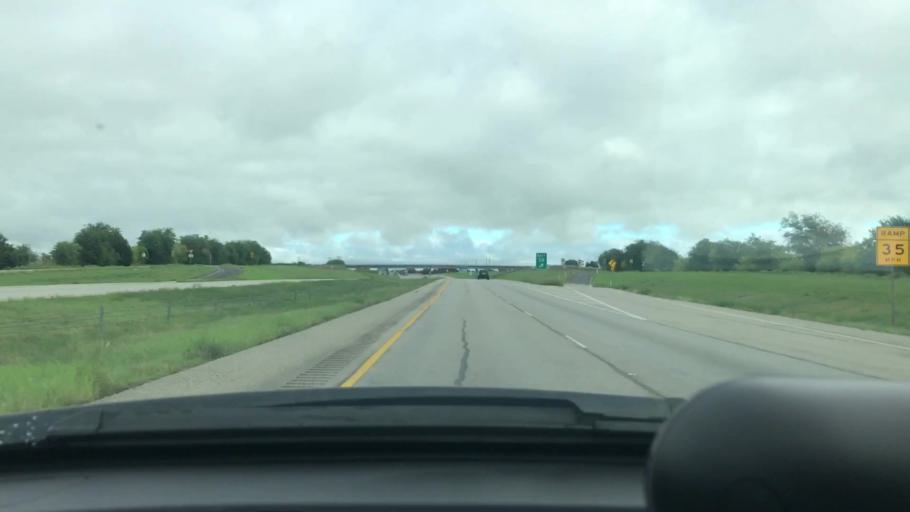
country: US
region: Texas
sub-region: Grayson County
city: Van Alstyne
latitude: 33.3964
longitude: -96.5803
